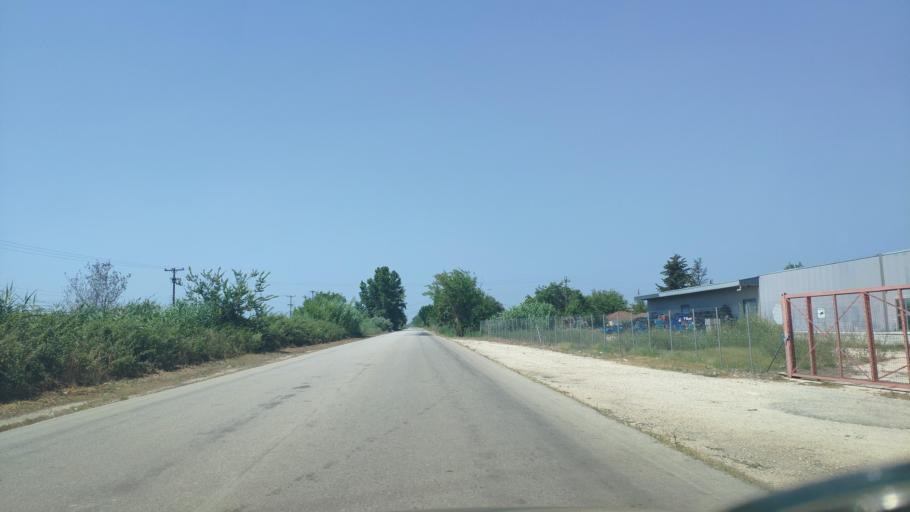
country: GR
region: Epirus
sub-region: Nomos Artas
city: Aneza
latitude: 39.1141
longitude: 20.9277
